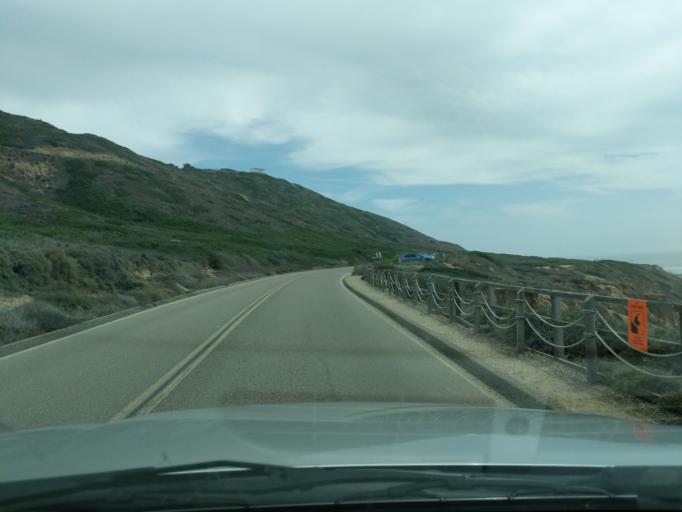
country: US
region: California
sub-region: San Diego County
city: Coronado
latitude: 32.6746
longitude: -117.2453
